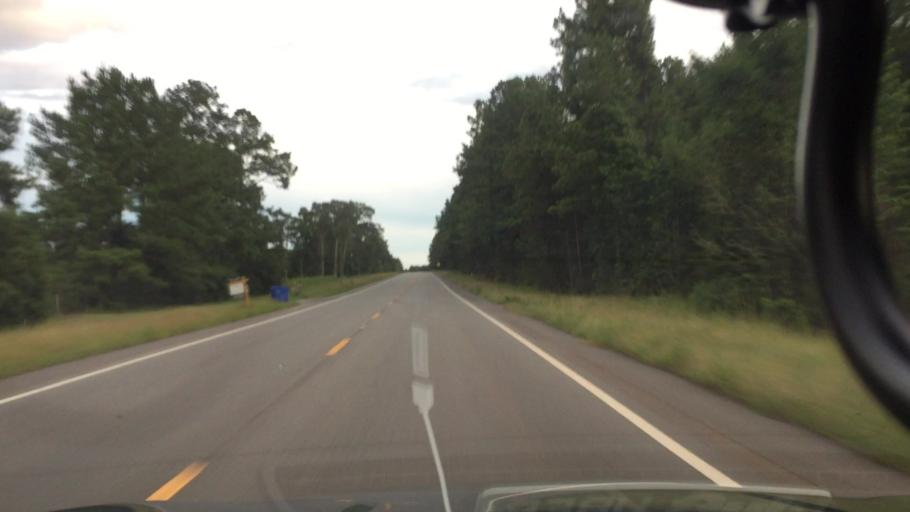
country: US
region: Alabama
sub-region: Pike County
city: Brundidge
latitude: 31.6094
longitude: -85.9465
